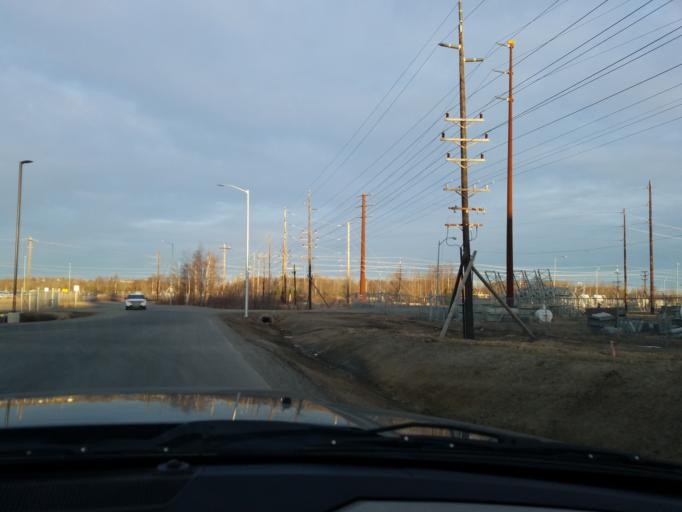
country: US
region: Alaska
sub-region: Anchorage Municipality
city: Anchorage
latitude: 61.1664
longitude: -149.9099
